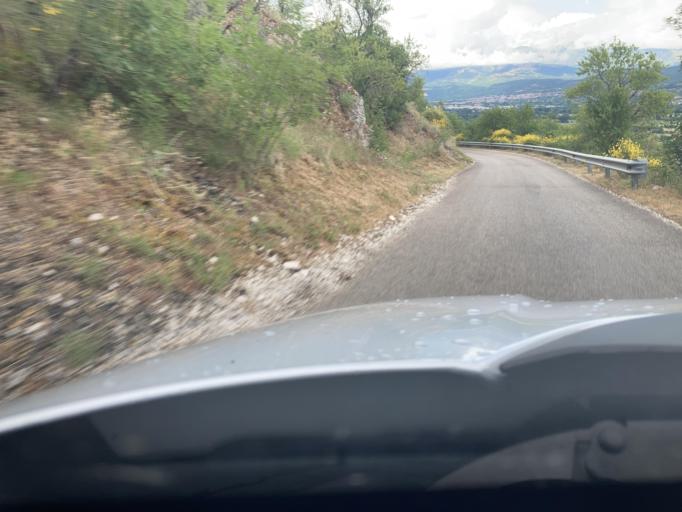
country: IT
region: Abruzzo
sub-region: Provincia dell' Aquila
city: Fossa
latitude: 42.2879
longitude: 13.4915
